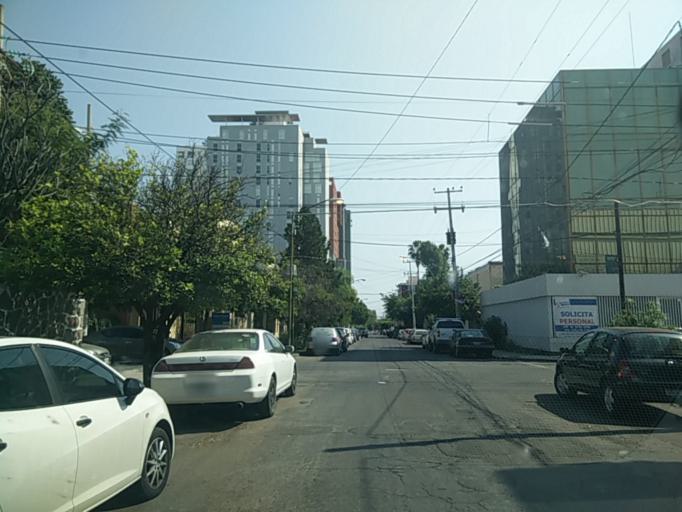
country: MX
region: Jalisco
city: Guadalajara
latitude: 20.6676
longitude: -103.3717
